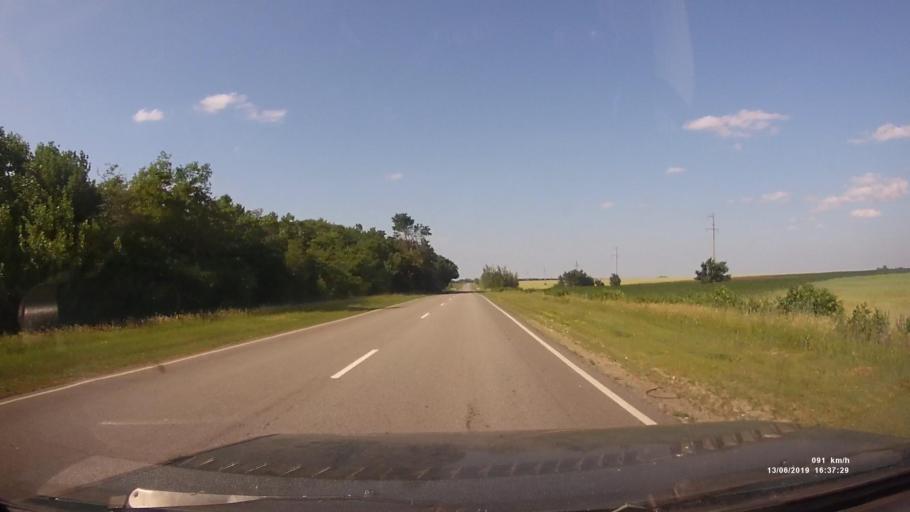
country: RU
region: Rostov
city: Kazanskaya
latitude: 49.9076
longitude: 41.3137
